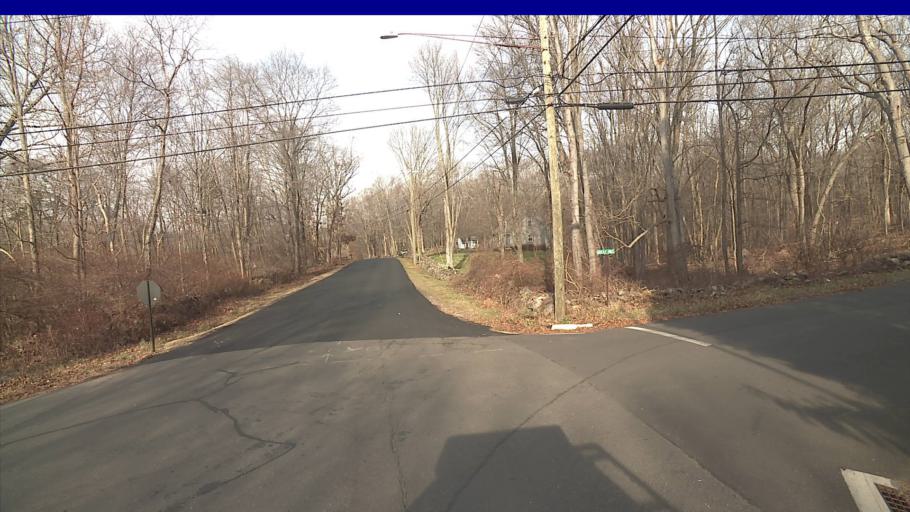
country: US
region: Connecticut
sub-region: Fairfield County
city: Newtown
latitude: 41.4003
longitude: -73.3577
